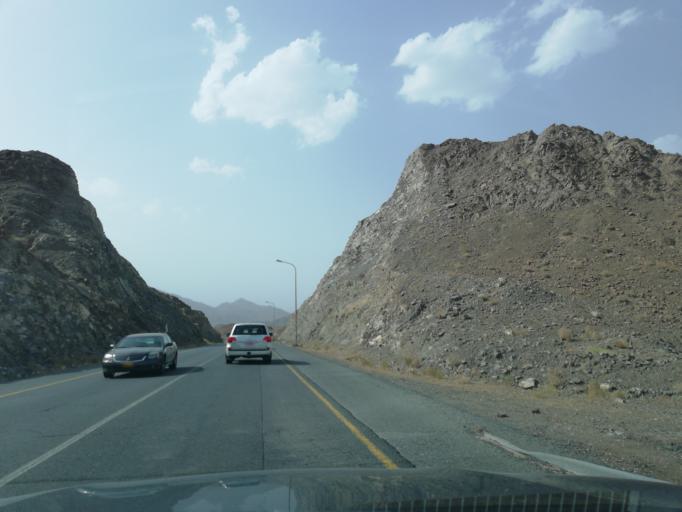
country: OM
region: Muhafazat ad Dakhiliyah
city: Sufalat Sama'il
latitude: 23.1960
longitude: 58.0852
